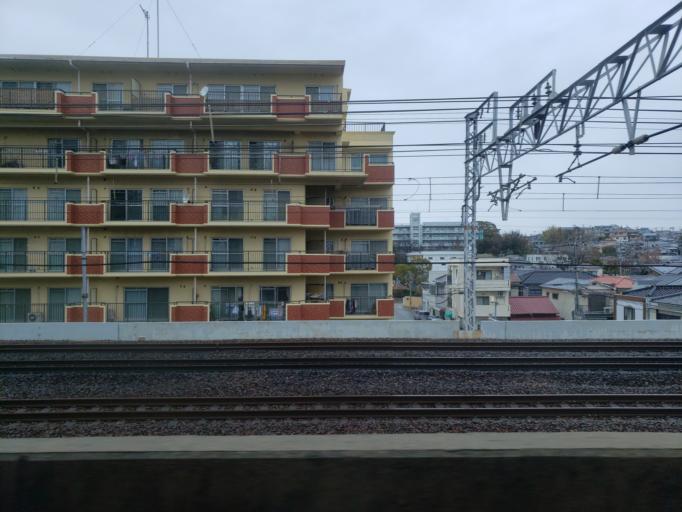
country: JP
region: Hyogo
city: Akashi
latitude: 34.6483
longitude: 134.9977
